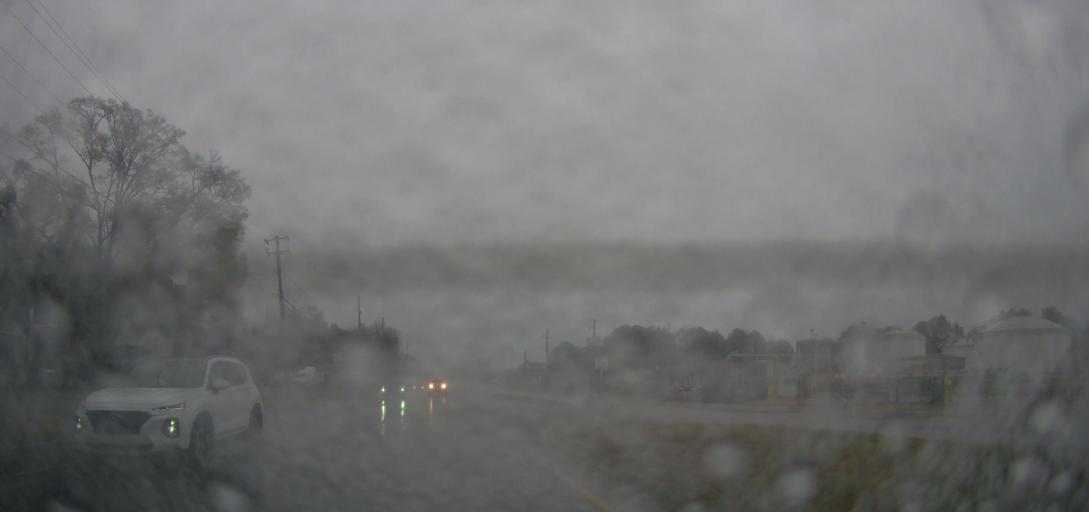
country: US
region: Alabama
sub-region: Autauga County
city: Prattville
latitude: 32.4028
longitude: -86.4028
